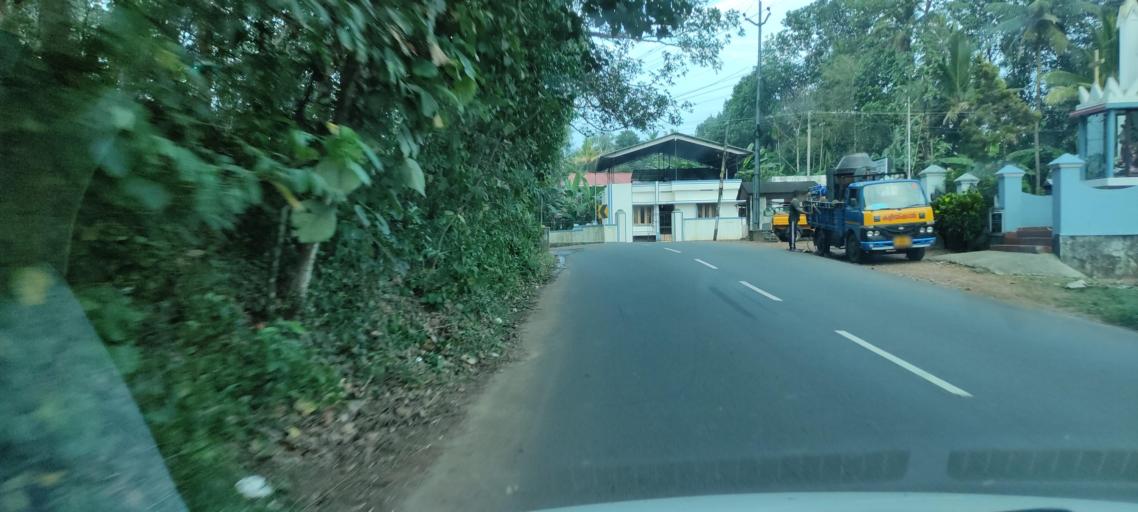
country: IN
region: Kerala
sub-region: Pattanamtitta
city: Adur
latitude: 9.1244
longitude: 76.7031
